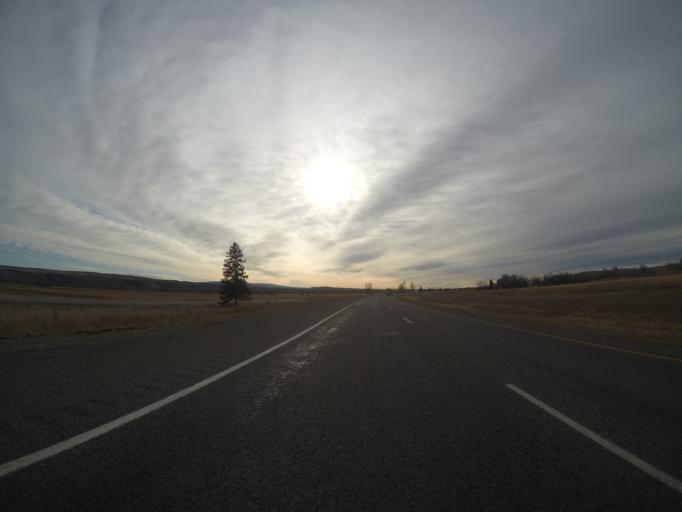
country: US
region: Montana
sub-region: Yellowstone County
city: Laurel
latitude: 45.5352
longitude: -108.8505
